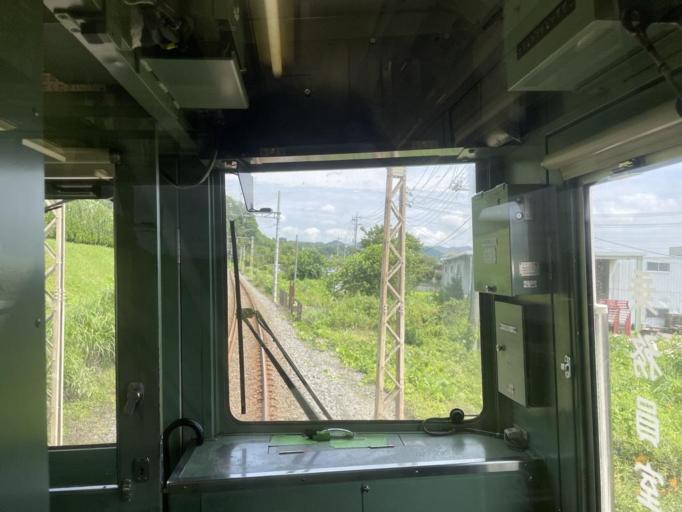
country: JP
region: Tochigi
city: Tanuma
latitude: 36.3933
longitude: 139.6035
